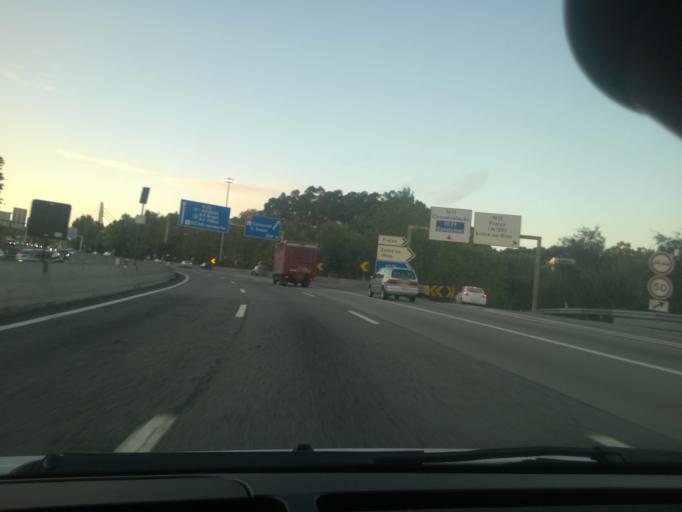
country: PT
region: Porto
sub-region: Gondomar
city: Valbom
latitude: 41.1501
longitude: -8.5789
